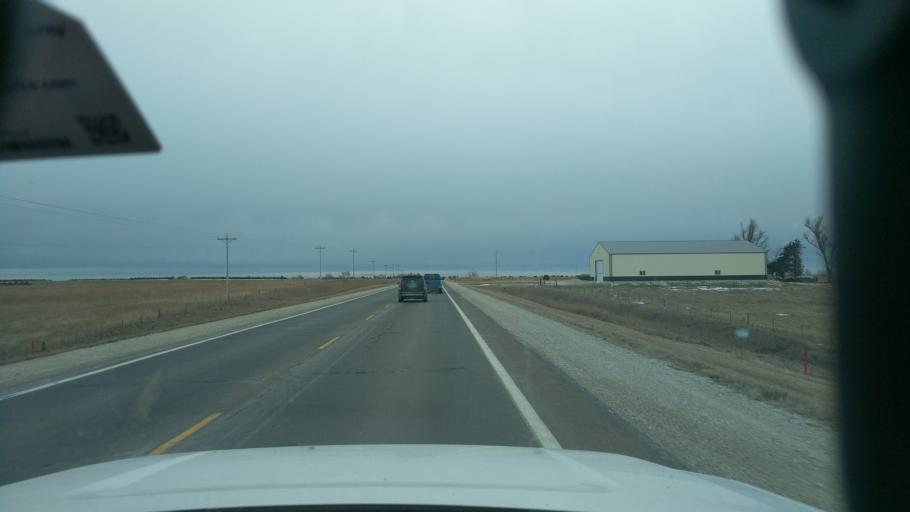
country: US
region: Kansas
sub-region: Dickinson County
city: Herington
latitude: 38.6237
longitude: -96.9487
